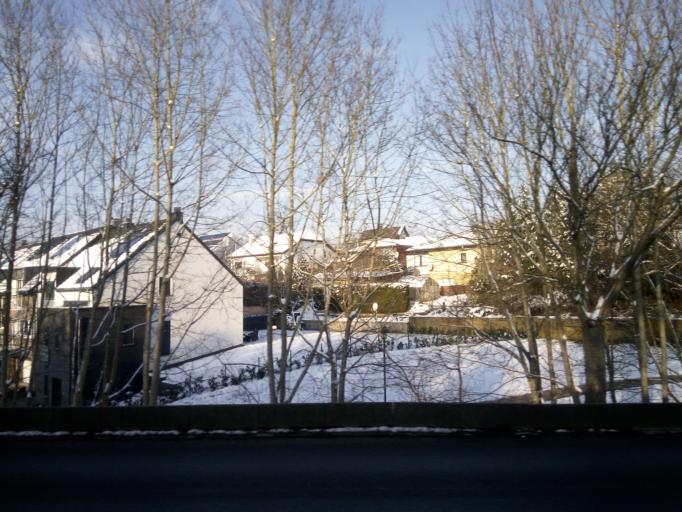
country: LU
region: Grevenmacher
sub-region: Canton de Grevenmacher
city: Junglinster
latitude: 49.7074
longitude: 6.2495
